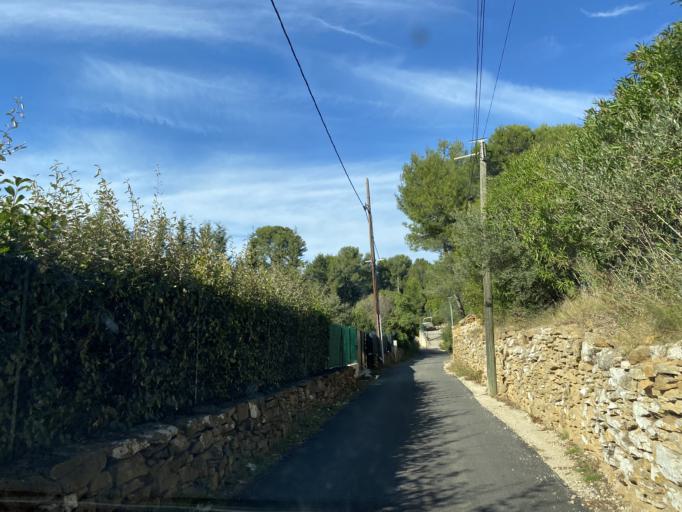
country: FR
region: Provence-Alpes-Cote d'Azur
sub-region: Departement des Bouches-du-Rhone
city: Ceyreste
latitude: 43.2071
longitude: 5.6040
